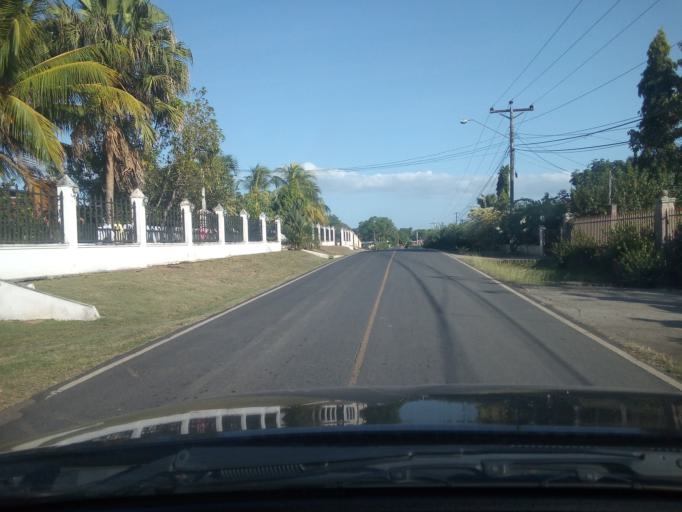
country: PA
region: Veraguas
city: Atalaya
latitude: 8.0459
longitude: -80.9314
